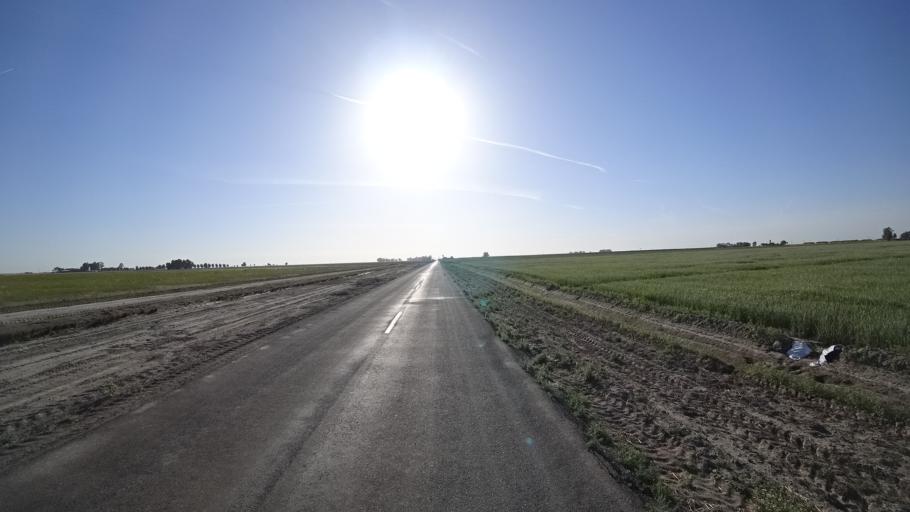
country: US
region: California
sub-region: Kings County
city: Stratford
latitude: 36.1673
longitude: -119.7916
